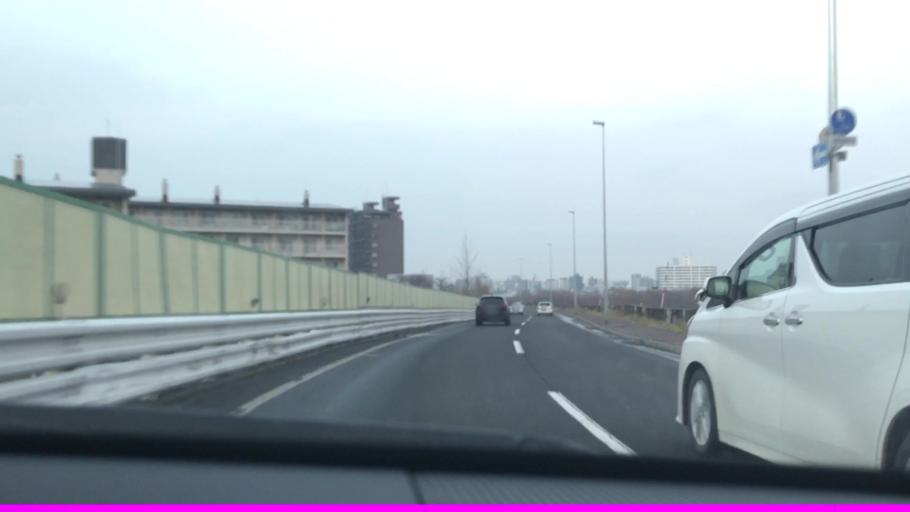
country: JP
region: Hokkaido
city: Sapporo
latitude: 43.0221
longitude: 141.3506
